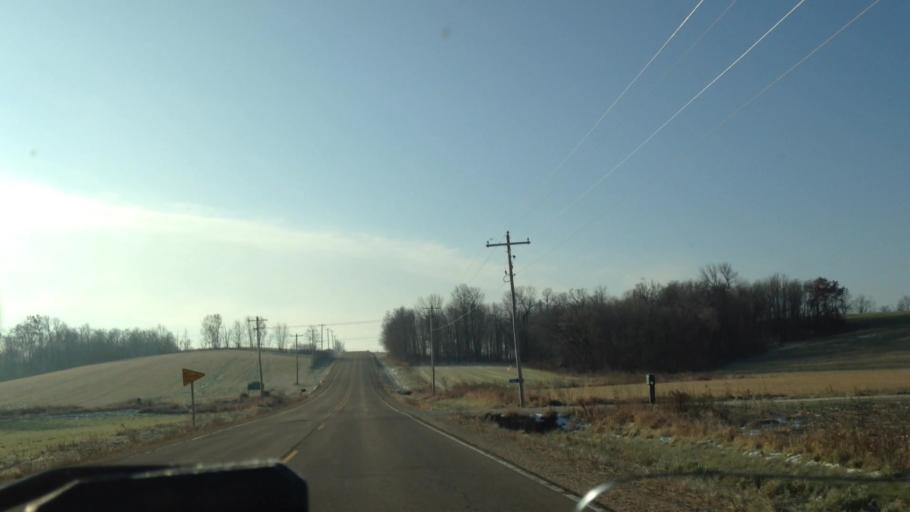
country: US
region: Wisconsin
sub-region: Dodge County
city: Mayville
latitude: 43.4636
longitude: -88.5000
